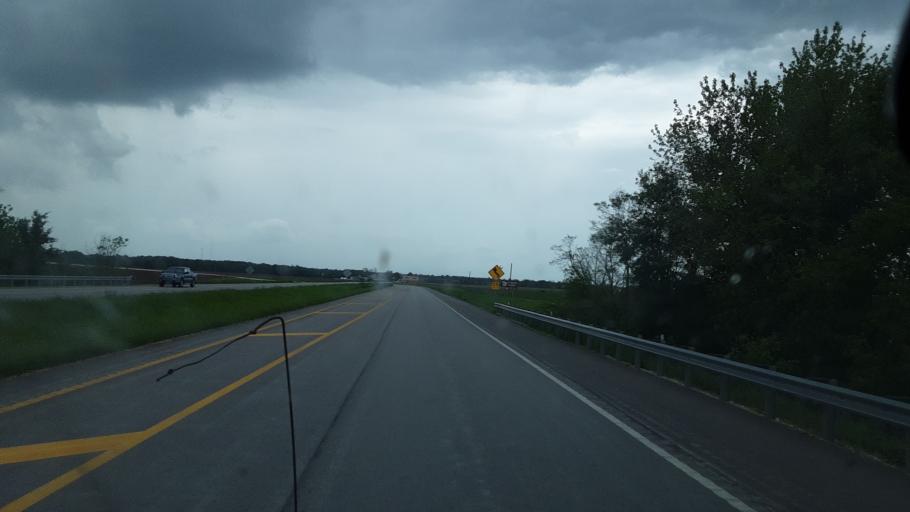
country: US
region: Missouri
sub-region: Marion County
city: Palmyra
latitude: 39.7384
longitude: -91.5102
